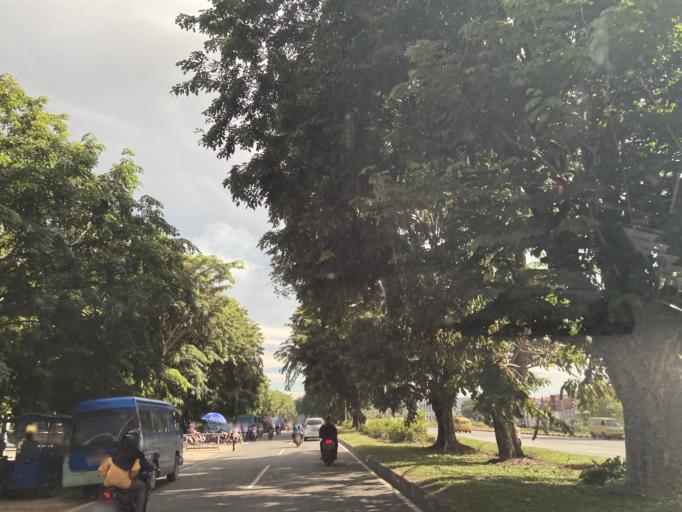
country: SG
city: Singapore
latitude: 1.1153
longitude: 104.0445
